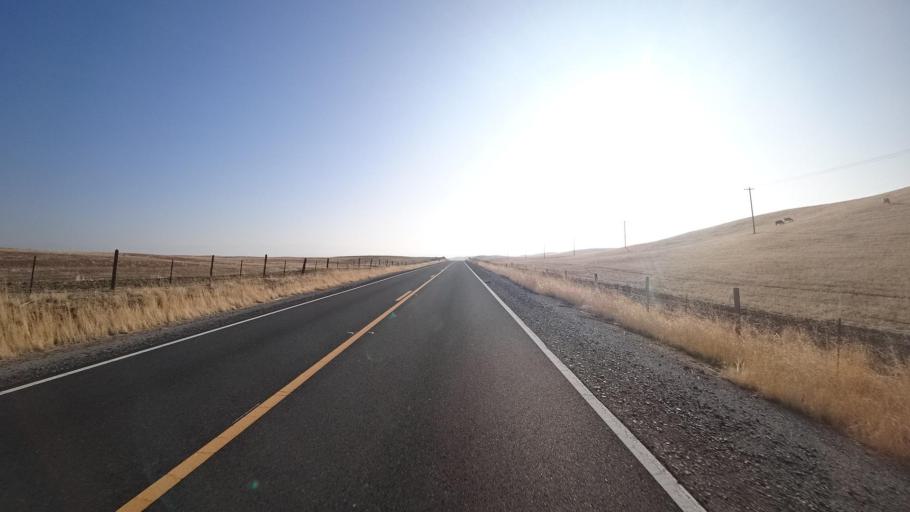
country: US
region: California
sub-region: Tulare County
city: Richgrove
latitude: 35.7548
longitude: -119.0168
